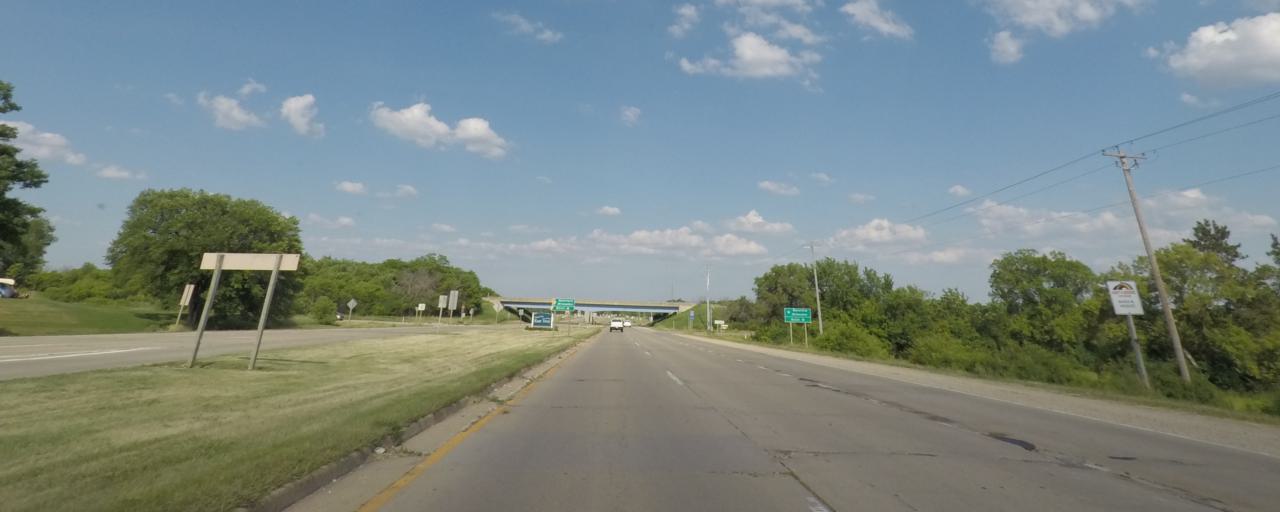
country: US
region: Wisconsin
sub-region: Walworth County
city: East Troy
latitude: 42.7921
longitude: -88.3882
